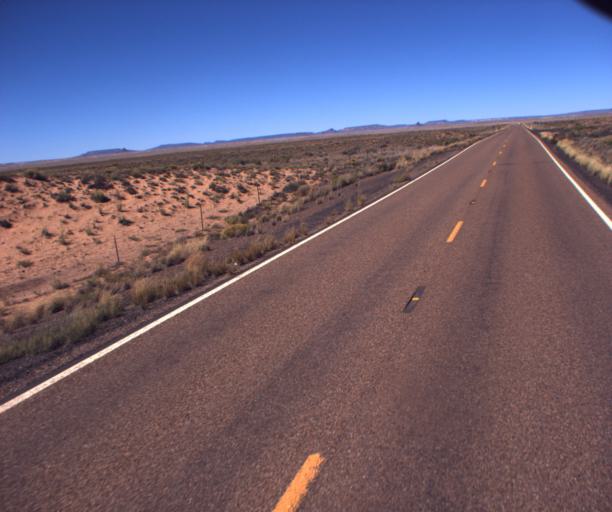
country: US
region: Arizona
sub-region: Navajo County
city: Holbrook
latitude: 35.0409
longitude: -110.0921
